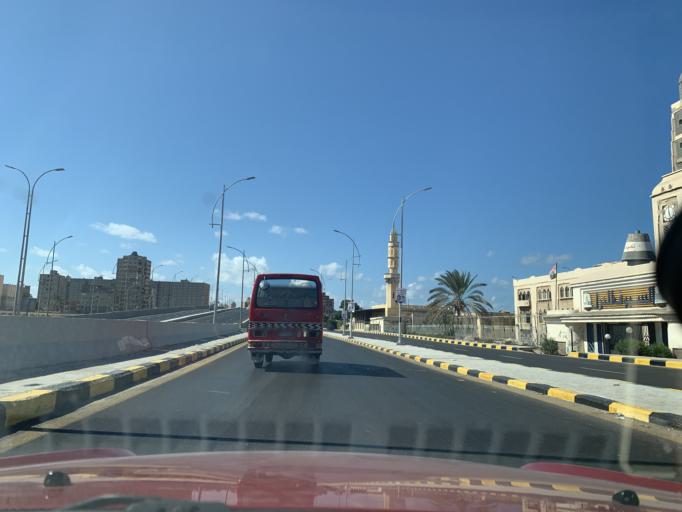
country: EG
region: Alexandria
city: Alexandria
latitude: 31.2228
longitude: 29.9870
